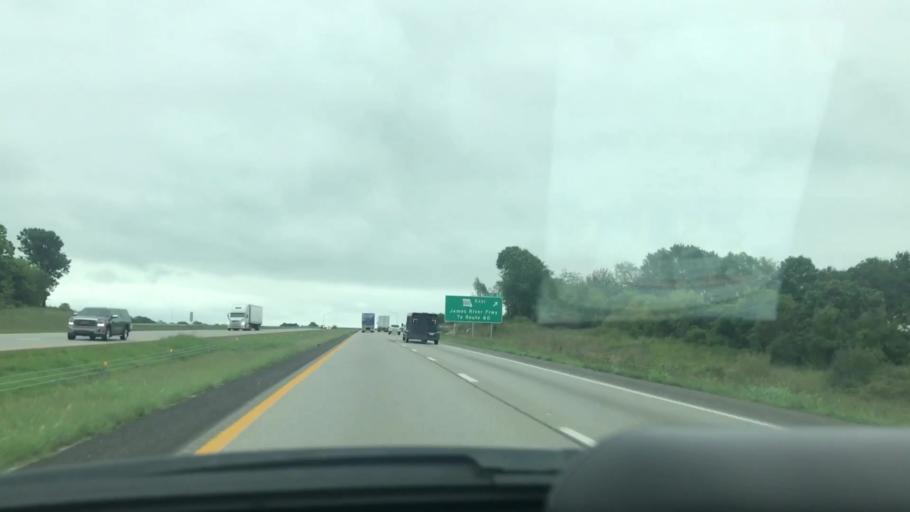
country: US
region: Missouri
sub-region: Greene County
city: Republic
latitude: 37.1942
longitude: -93.4528
